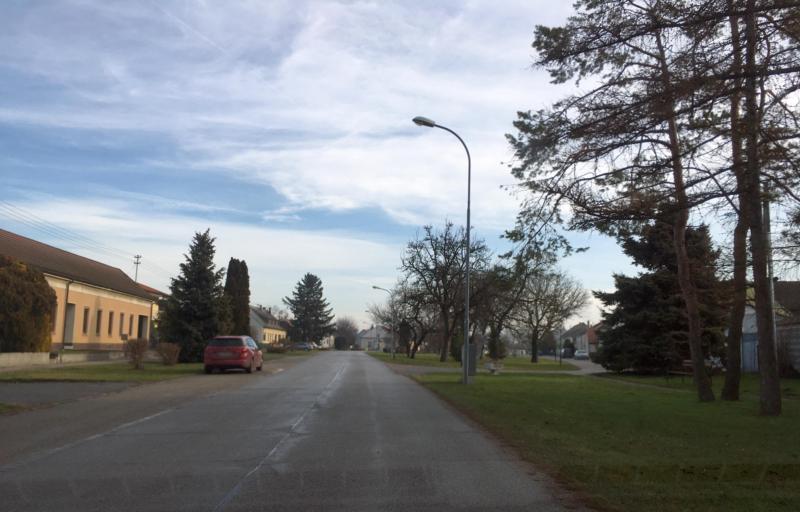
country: AT
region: Lower Austria
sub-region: Politischer Bezirk Ganserndorf
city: Haringsee
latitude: 48.1829
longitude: 16.7375
